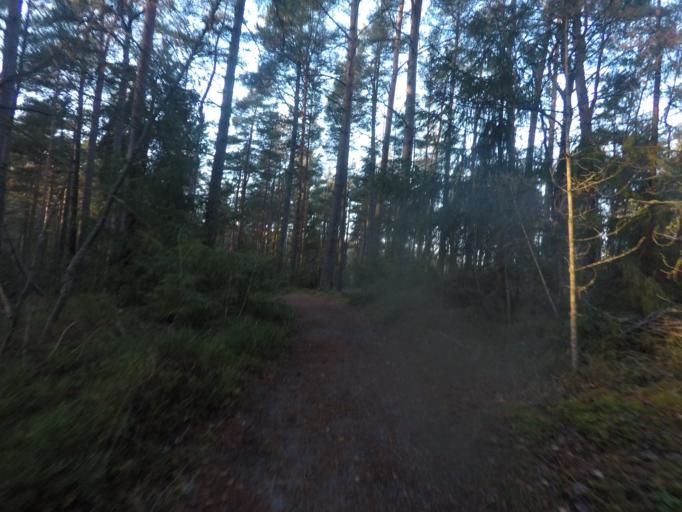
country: SE
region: Soedermanland
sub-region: Eskilstuna Kommun
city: Eskilstuna
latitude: 59.3897
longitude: 16.5280
